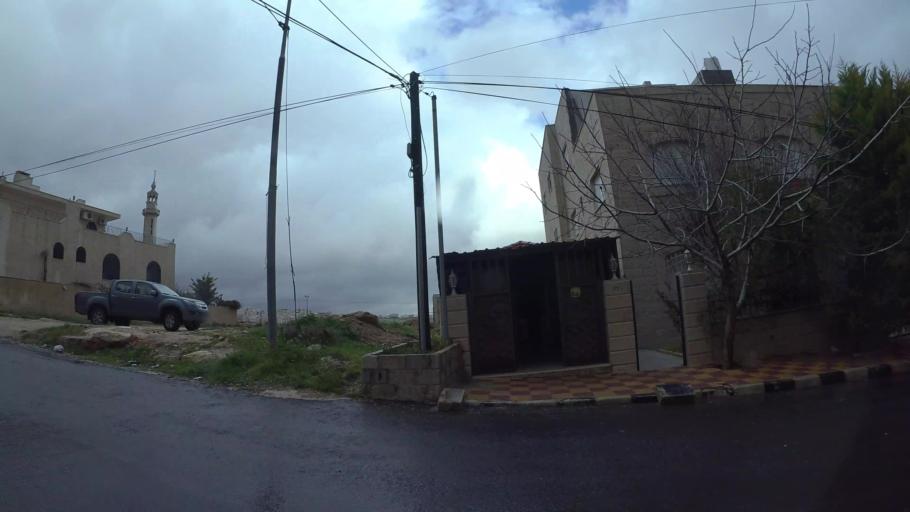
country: JO
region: Amman
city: Al Jubayhah
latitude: 32.0361
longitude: 35.8916
